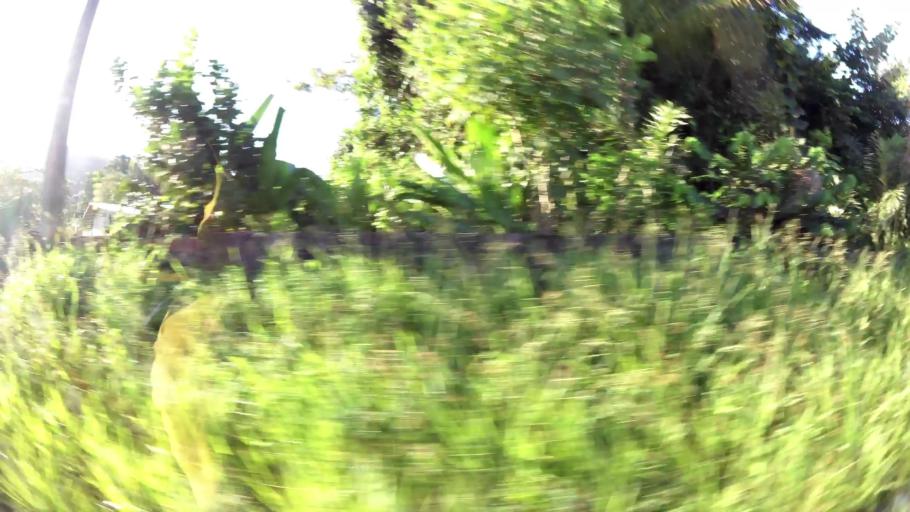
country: GF
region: Guyane
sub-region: Guyane
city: Remire-Montjoly
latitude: 4.8886
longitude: -52.2930
